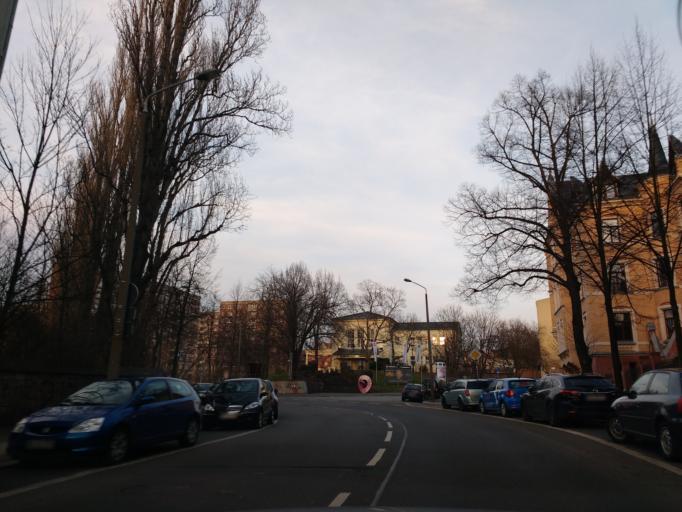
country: DE
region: Saxony-Anhalt
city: Halle (Saale)
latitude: 51.4743
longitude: 11.9734
